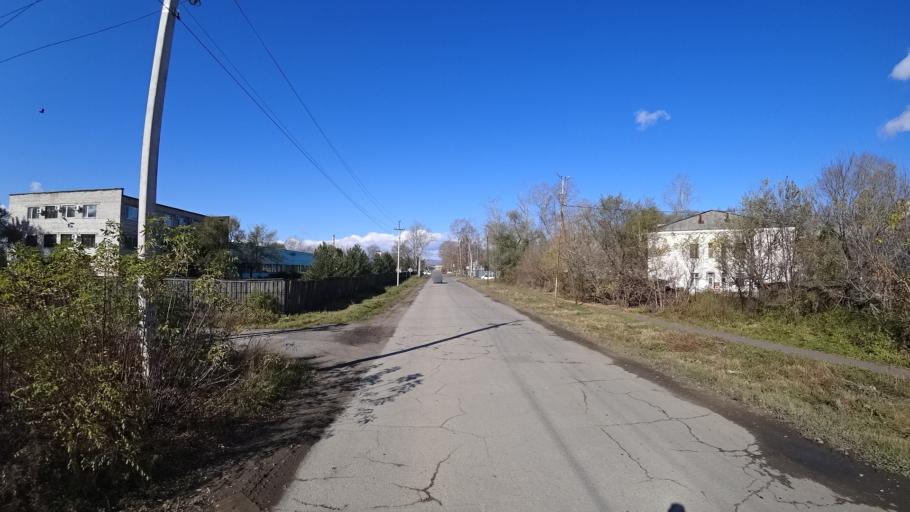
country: RU
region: Khabarovsk Krai
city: Amursk
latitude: 50.0980
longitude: 136.4933
